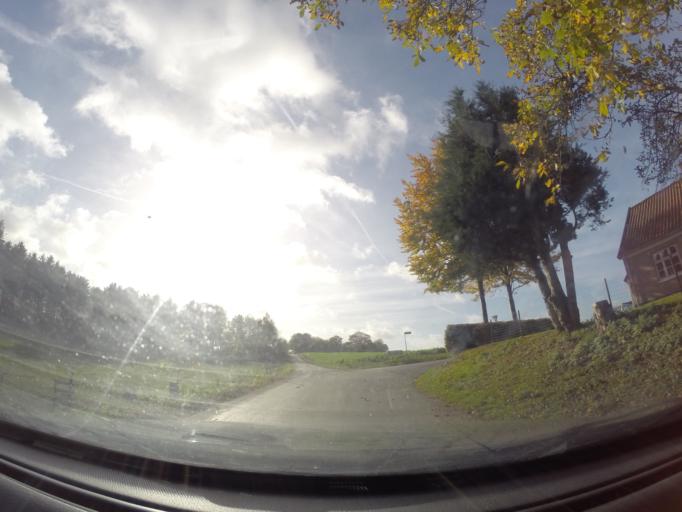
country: DK
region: South Denmark
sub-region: Faaborg-Midtfyn Kommune
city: Ringe
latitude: 55.2123
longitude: 10.5614
